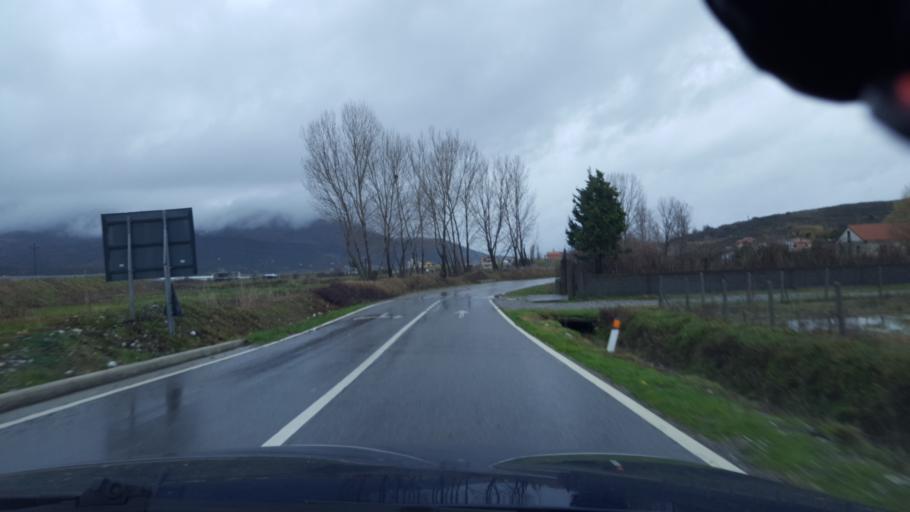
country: AL
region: Shkoder
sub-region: Rrethi i Shkodres
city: Berdica e Madhe
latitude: 42.0060
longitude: 19.4796
